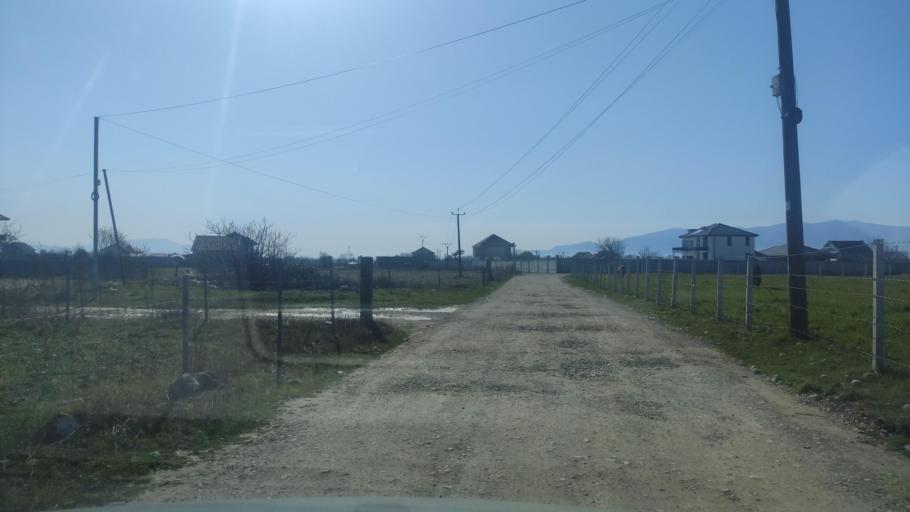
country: AL
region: Shkoder
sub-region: Rrethi i Malesia e Madhe
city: Grude-Fushe
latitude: 42.1605
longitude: 19.4582
